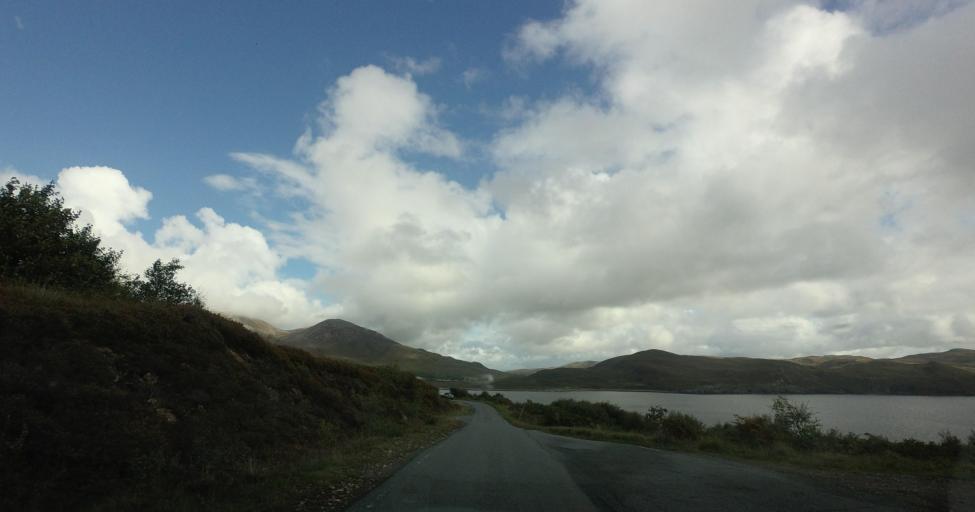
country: GB
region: Scotland
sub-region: Highland
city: Portree
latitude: 57.1946
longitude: -6.0303
